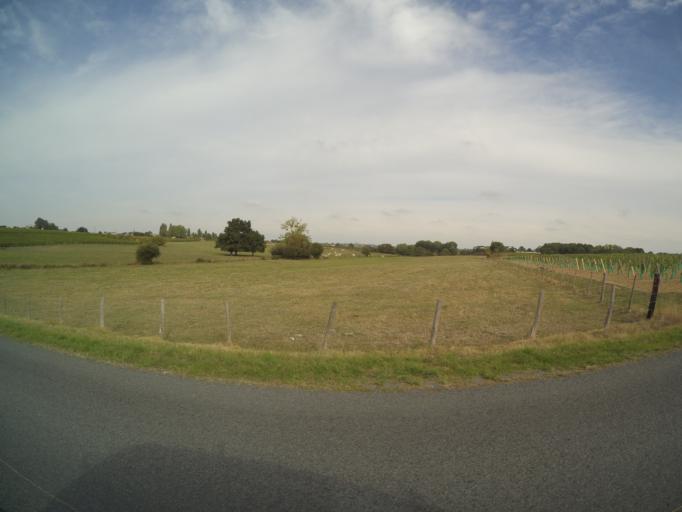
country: FR
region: Pays de la Loire
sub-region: Departement de Maine-et-Loire
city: Martigne-Briand
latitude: 47.2024
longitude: -0.4403
